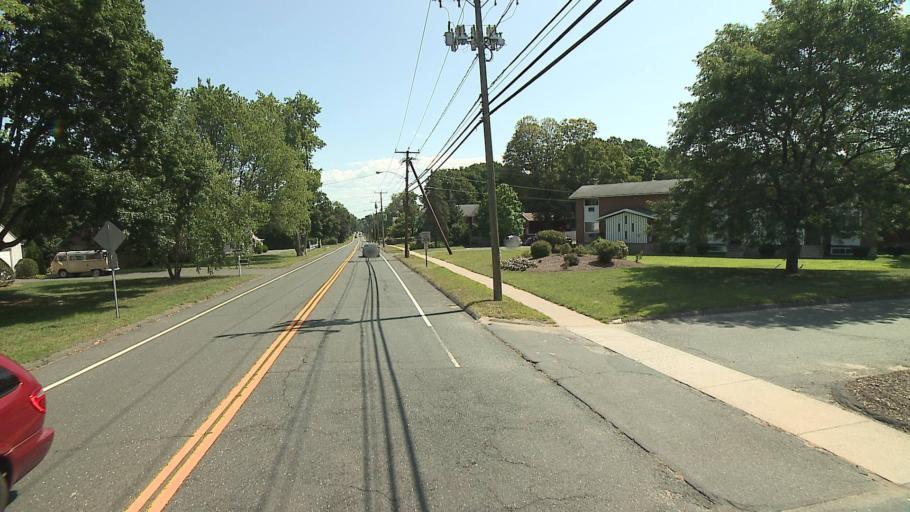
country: US
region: Connecticut
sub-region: Hartford County
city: Windsor Locks
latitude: 41.9263
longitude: -72.6462
